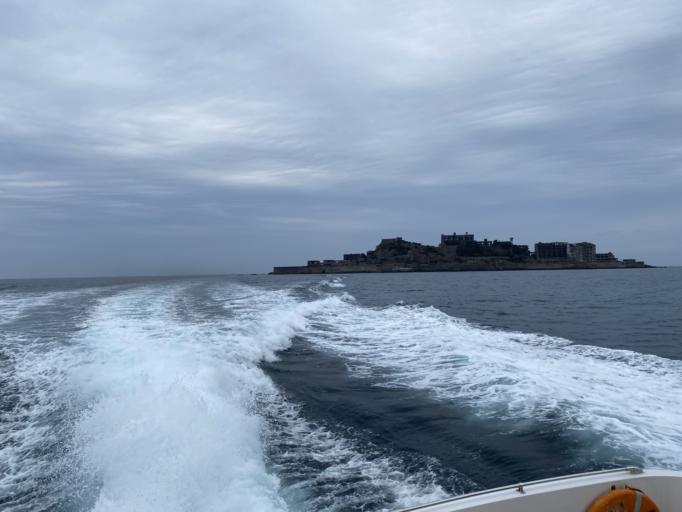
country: JP
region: Nagasaki
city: Nagasaki-shi
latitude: 32.6237
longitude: 129.7443
